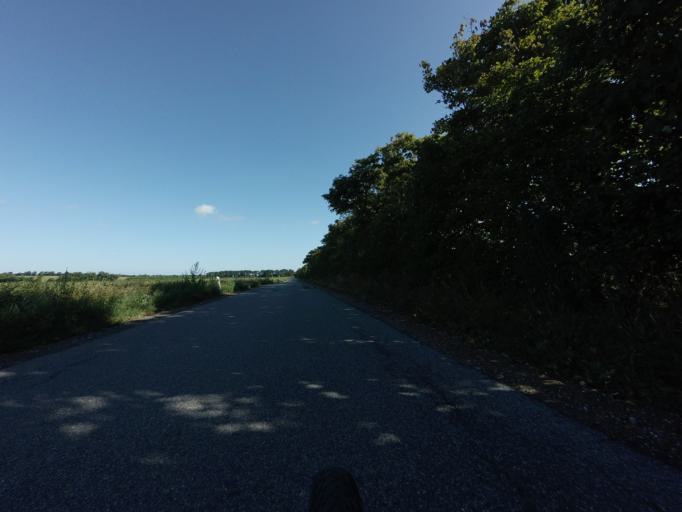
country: DK
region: North Denmark
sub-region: Hjorring Kommune
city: Vra
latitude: 57.3662
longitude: 10.0034
